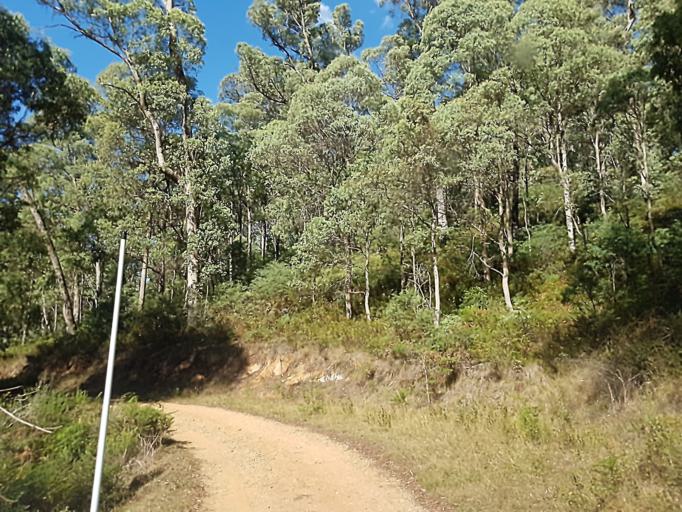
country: AU
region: Victoria
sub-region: Alpine
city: Mount Beauty
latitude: -36.9220
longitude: 147.0318
